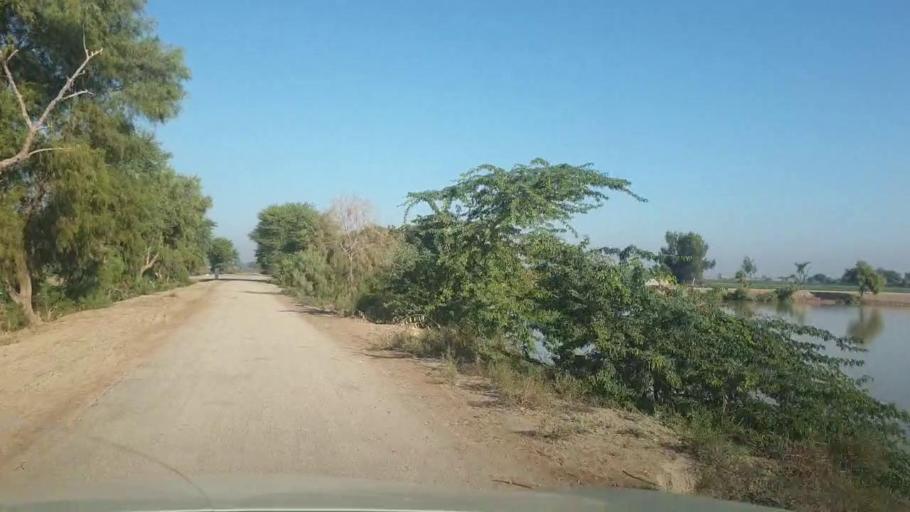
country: PK
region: Sindh
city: Bhan
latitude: 26.5404
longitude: 67.6894
